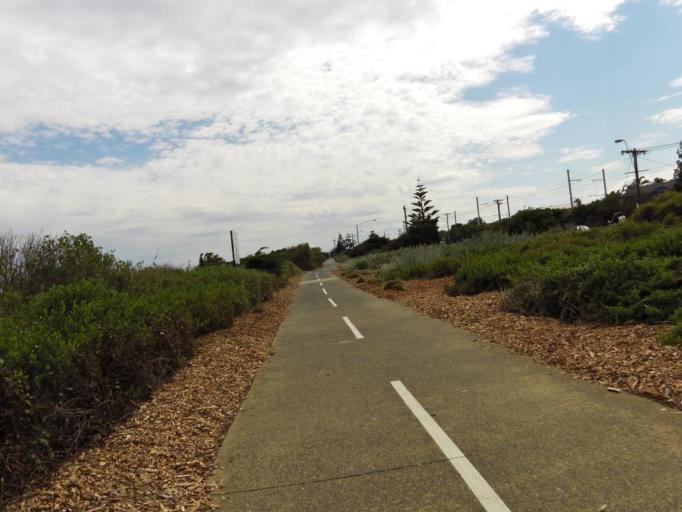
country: AU
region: Victoria
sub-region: Bayside
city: Hampton
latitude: -37.9338
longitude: 144.9944
